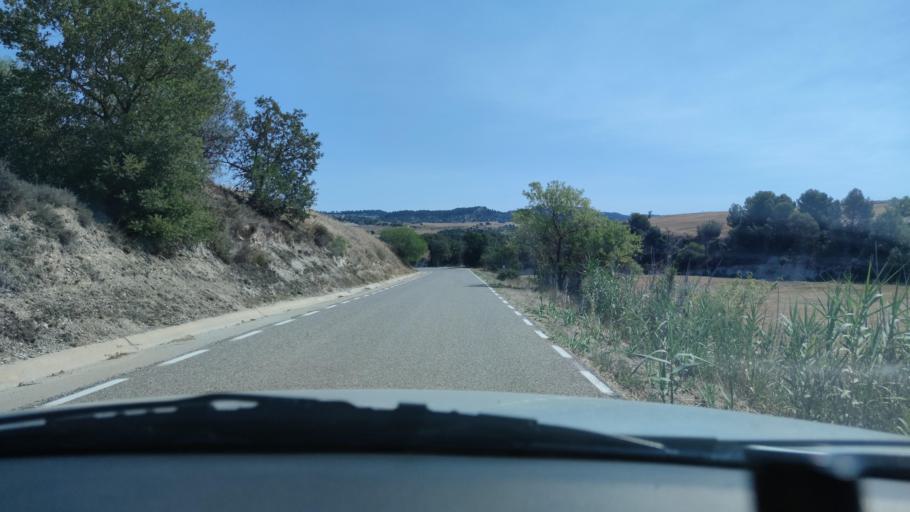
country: ES
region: Catalonia
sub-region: Provincia de Lleida
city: Cervera
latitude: 41.6293
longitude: 1.3275
